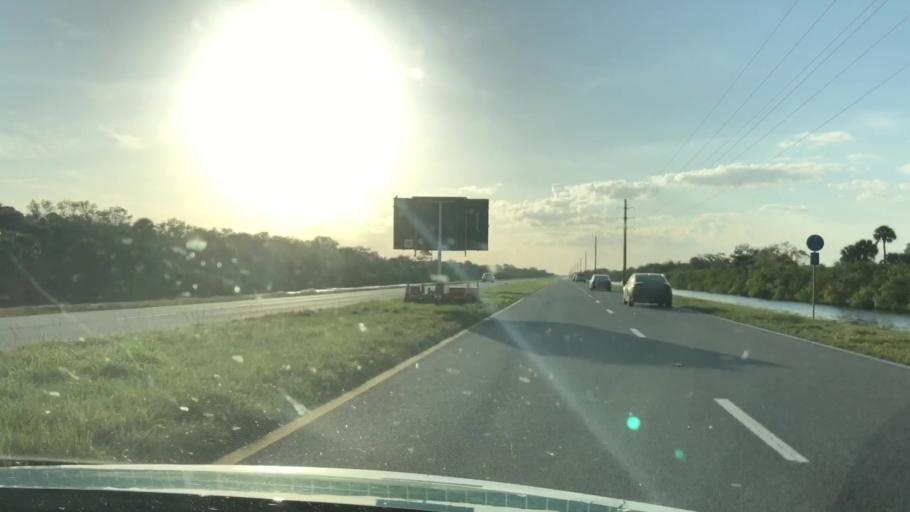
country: US
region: Florida
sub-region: Brevard County
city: Merritt Island
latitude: 28.5266
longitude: -80.7013
